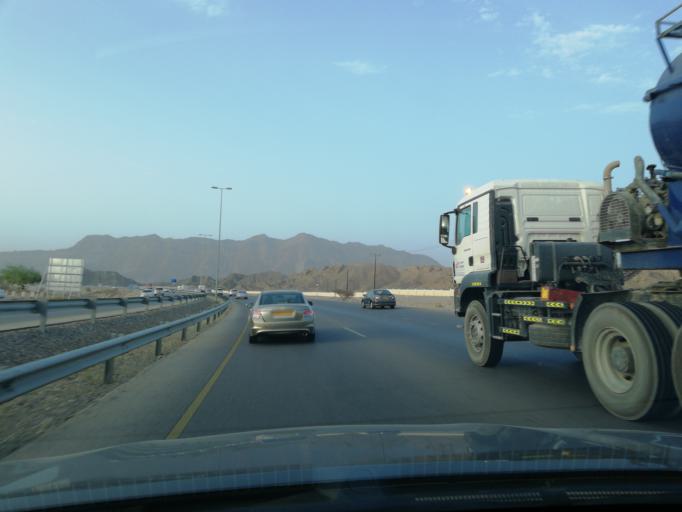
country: OM
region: Muhafazat ad Dakhiliyah
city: Bidbid
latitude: 23.4198
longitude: 58.1199
